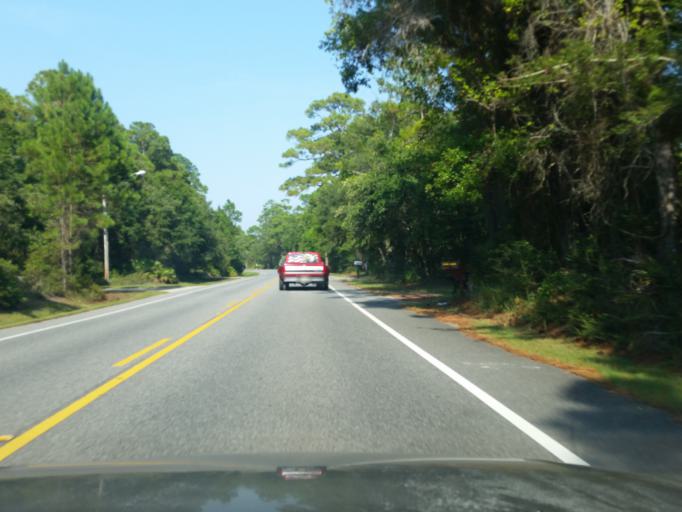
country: US
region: Alabama
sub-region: Baldwin County
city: Gulf Shores
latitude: 30.2467
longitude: -87.7777
